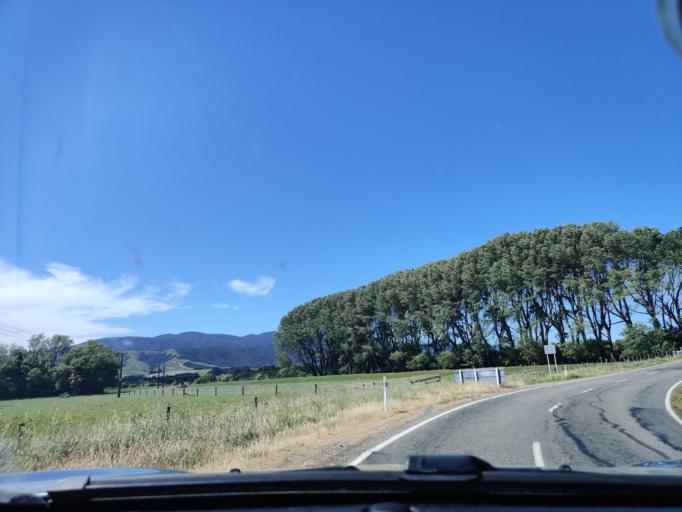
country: NZ
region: Wellington
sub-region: Upper Hutt City
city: Upper Hutt
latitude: -41.2855
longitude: 175.2693
